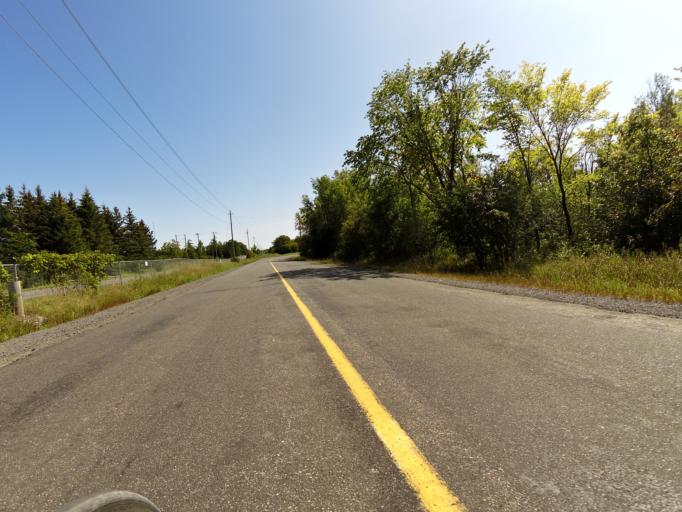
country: CA
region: Ontario
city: Bells Corners
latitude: 45.3582
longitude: -75.9129
